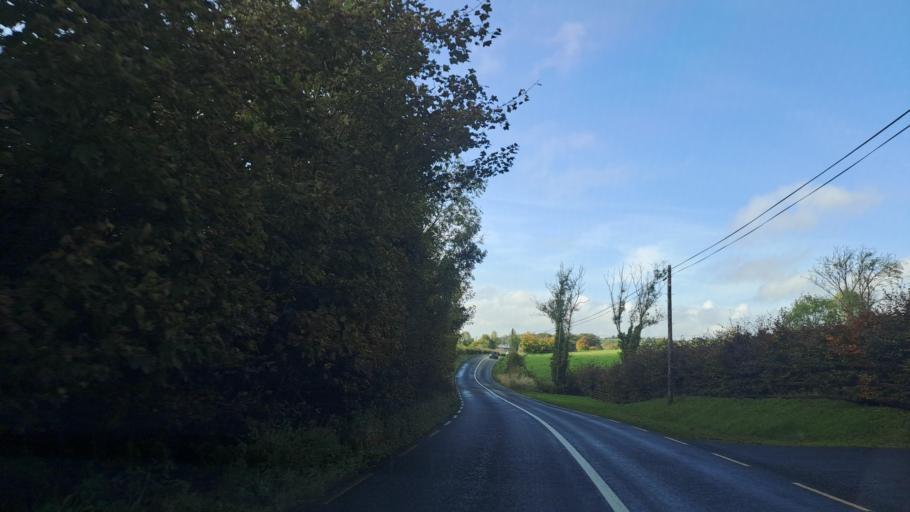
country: IE
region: Ulster
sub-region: An Cabhan
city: Cootehill
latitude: 54.0618
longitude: -7.0385
